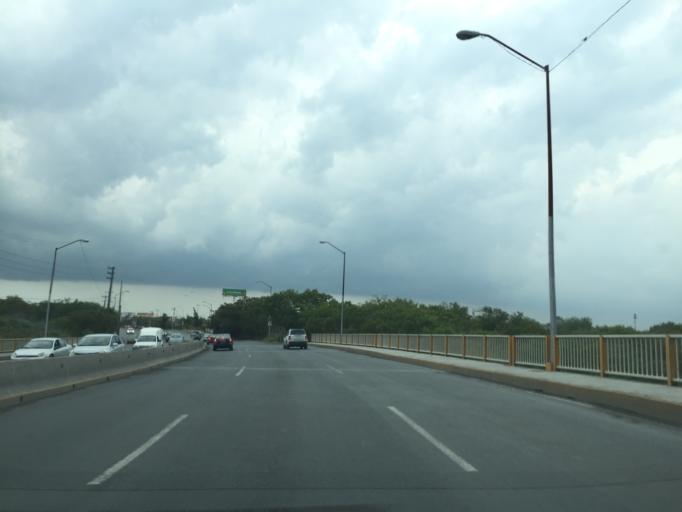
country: MX
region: Nuevo Leon
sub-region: Juarez
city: Valle de Juarez
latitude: 25.6741
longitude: -100.1679
